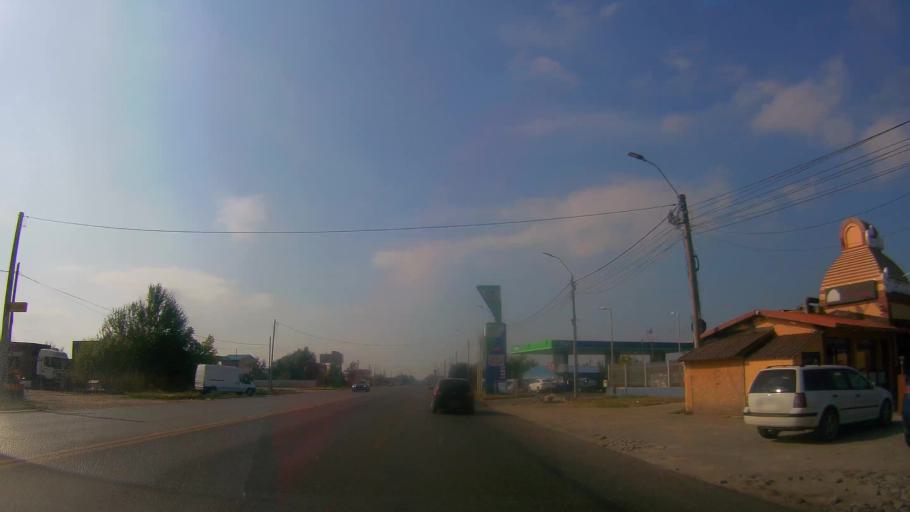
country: RO
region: Ilfov
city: Prim Decembrie
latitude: 44.3015
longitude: 26.0618
